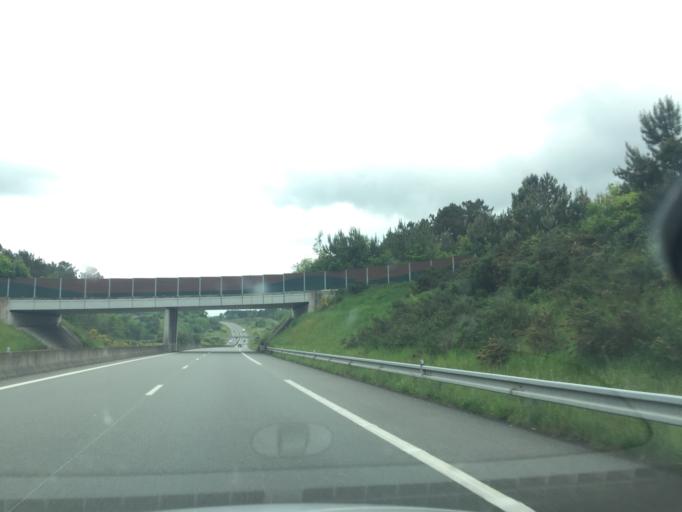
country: FR
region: Pays de la Loire
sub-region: Departement de la Sarthe
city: Luceau
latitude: 47.7183
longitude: 0.3447
